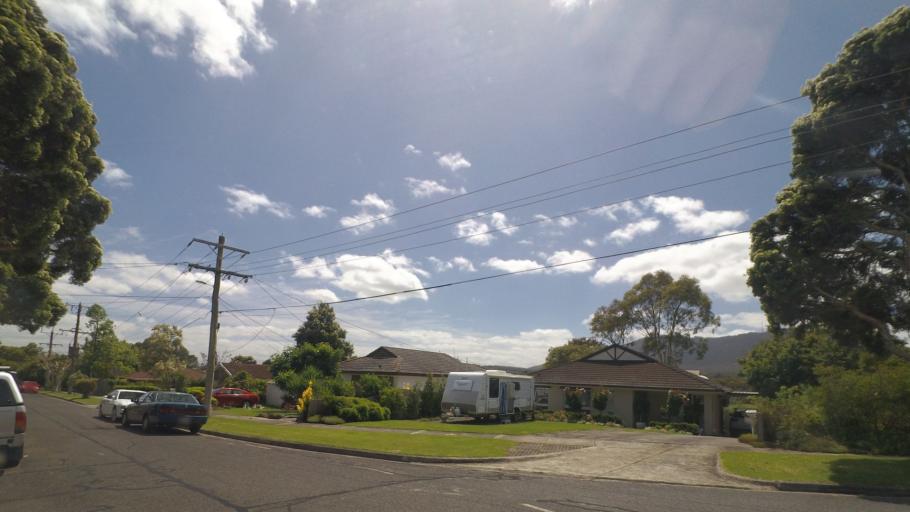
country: AU
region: Victoria
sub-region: Maroondah
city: Bayswater North
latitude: -37.8284
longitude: 145.3017
